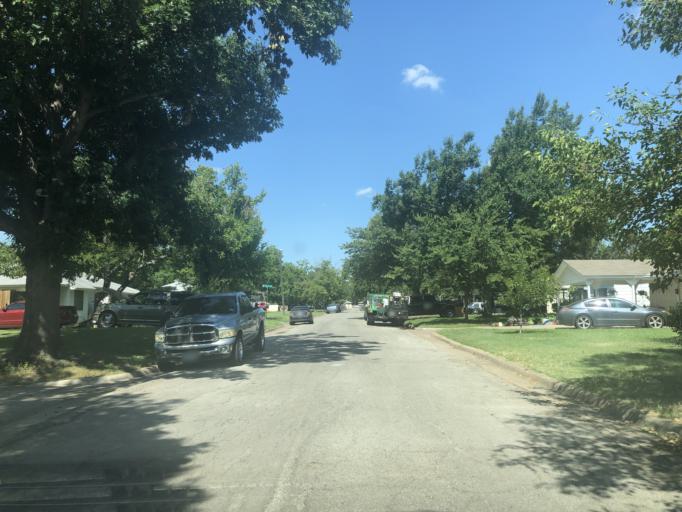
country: US
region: Texas
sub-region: Dallas County
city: Grand Prairie
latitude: 32.7365
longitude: -97.0106
